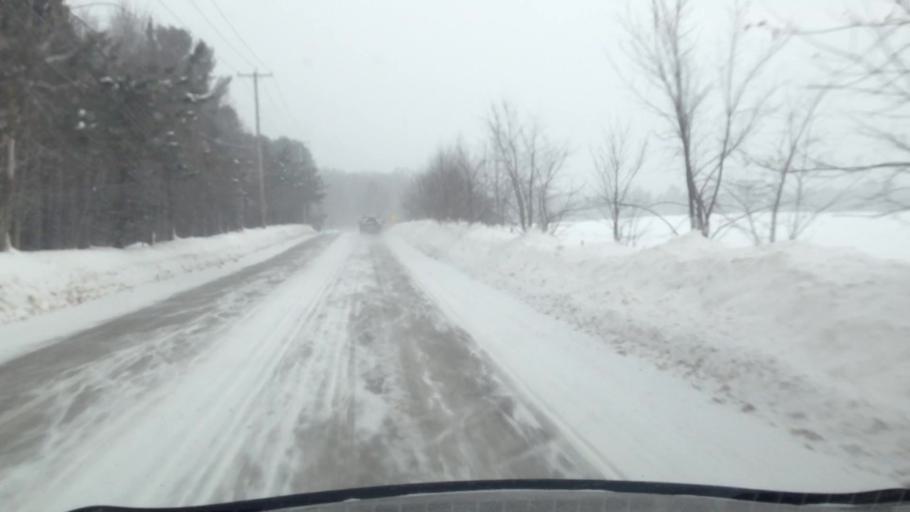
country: CA
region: Quebec
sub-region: Laurentides
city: Mont-Tremblant
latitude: 45.9698
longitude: -74.6285
